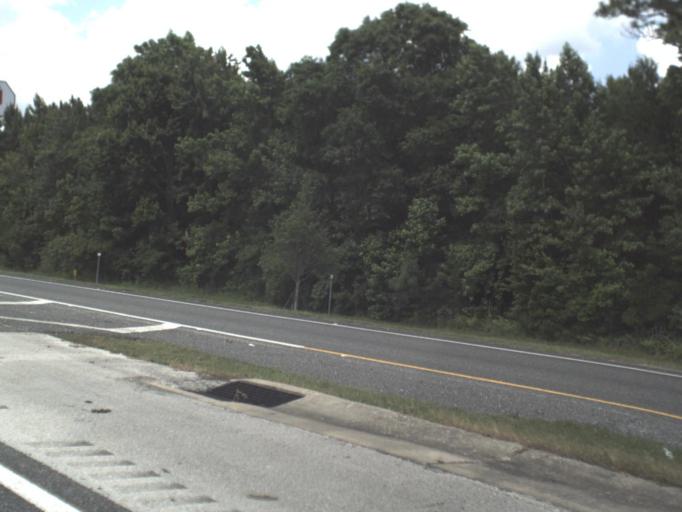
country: US
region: Florida
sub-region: Saint Johns County
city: Saint Augustine
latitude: 29.9201
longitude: -81.4127
